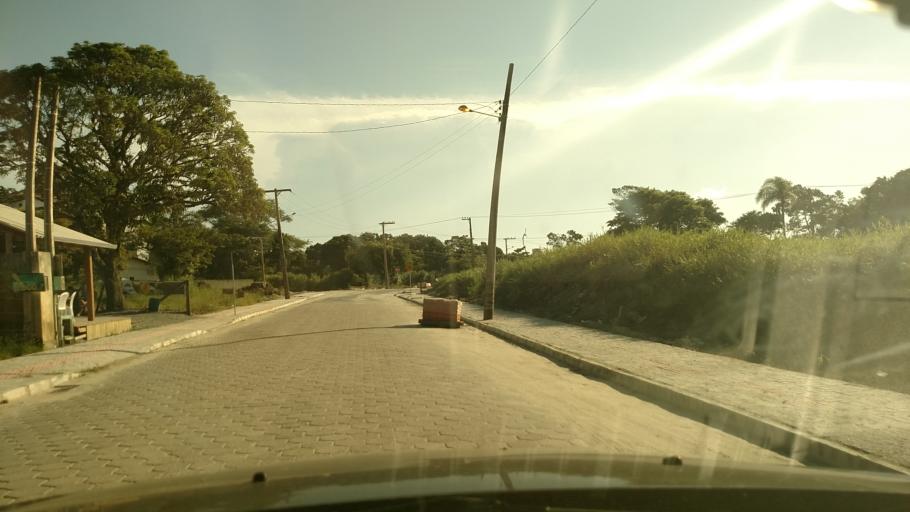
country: BR
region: Santa Catarina
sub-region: Porto Belo
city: Porto Belo
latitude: -27.1825
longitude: -48.5103
